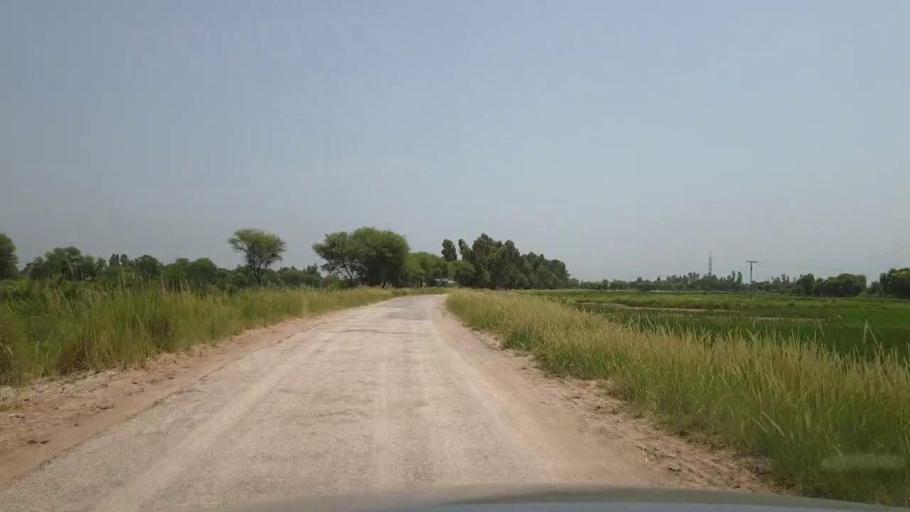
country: PK
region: Sindh
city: Ratodero
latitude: 27.8003
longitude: 68.3433
